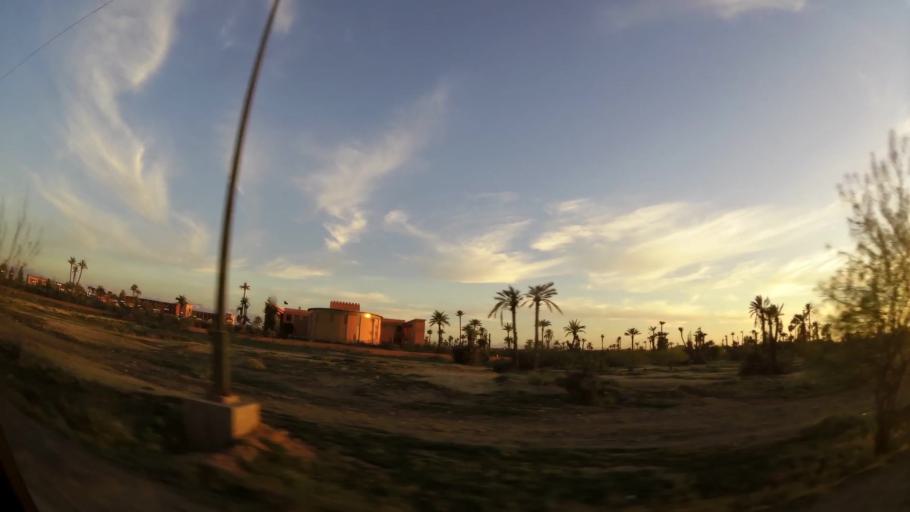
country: MA
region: Marrakech-Tensift-Al Haouz
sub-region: Marrakech
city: Marrakesh
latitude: 31.6870
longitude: -7.9947
